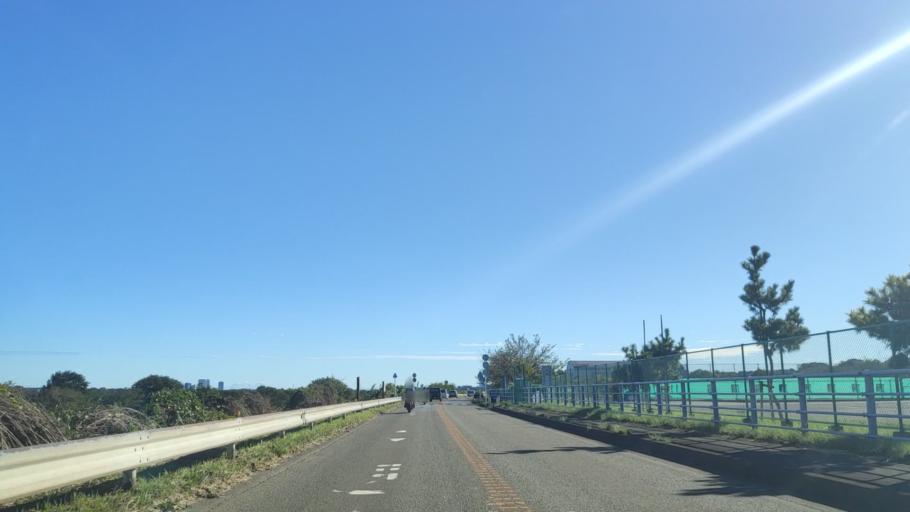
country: JP
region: Kanagawa
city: Zama
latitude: 35.5094
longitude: 139.3741
